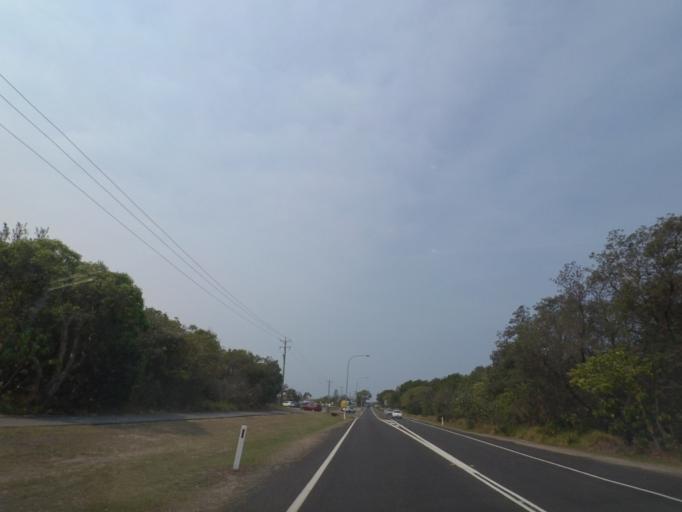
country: AU
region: New South Wales
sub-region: Tweed
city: Casuarina
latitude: -28.3398
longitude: 153.5724
